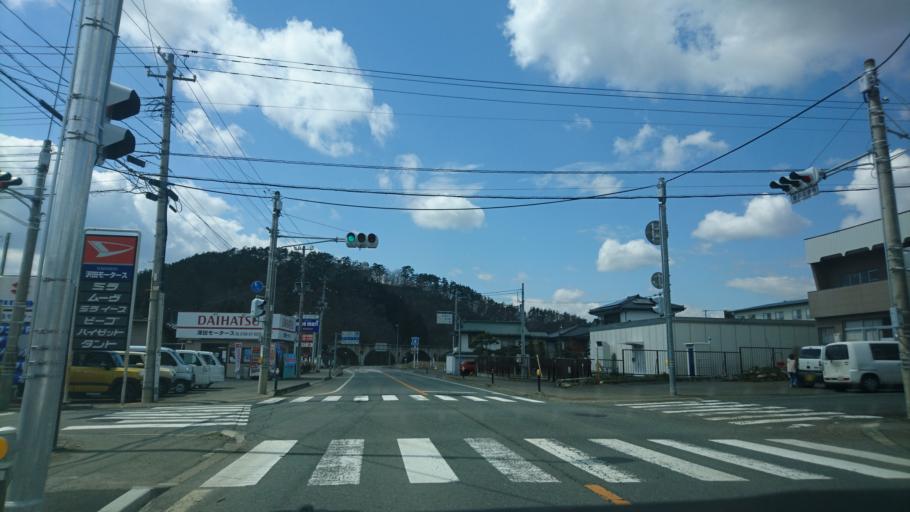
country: JP
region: Iwate
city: Tono
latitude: 39.3462
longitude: 141.3534
